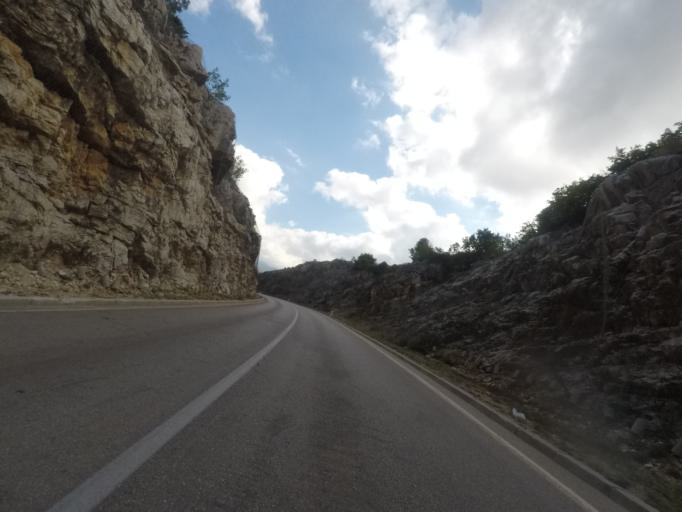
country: BA
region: Republika Srpska
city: Trebinje
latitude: 42.6491
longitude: 18.3696
